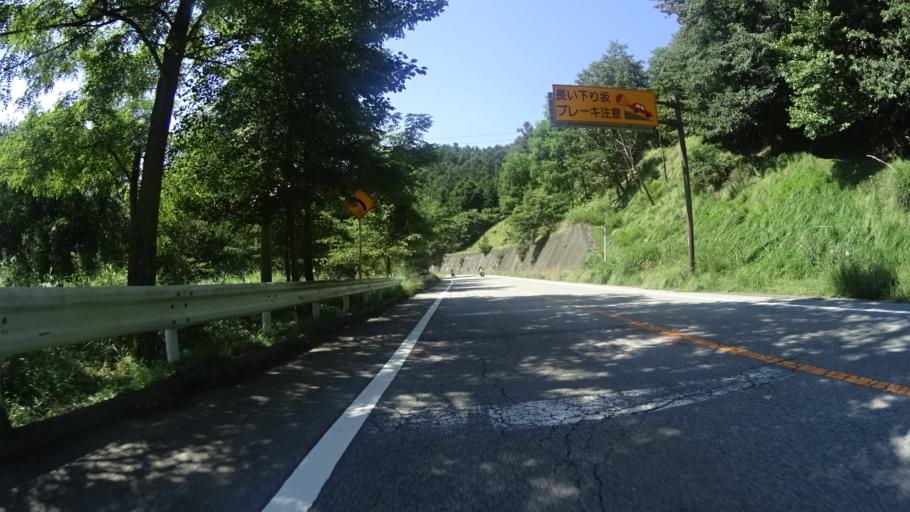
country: JP
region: Yamanashi
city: Enzan
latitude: 35.7500
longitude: 138.8068
